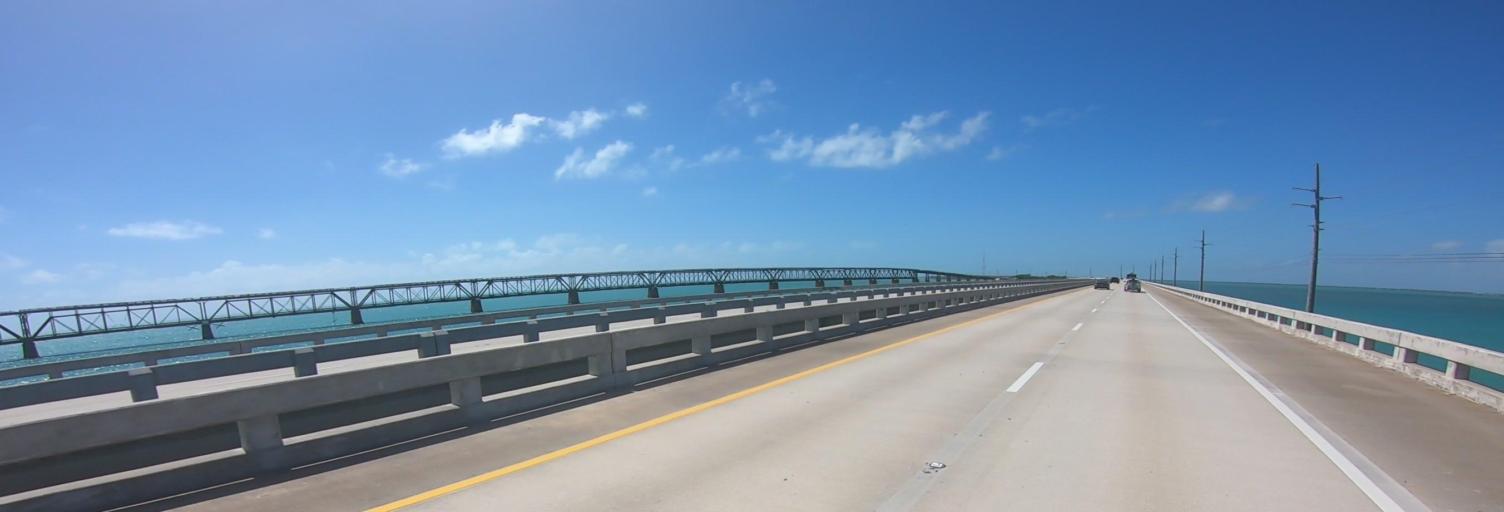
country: US
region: Florida
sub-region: Monroe County
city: Big Pine Key
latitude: 24.6586
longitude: -81.2895
